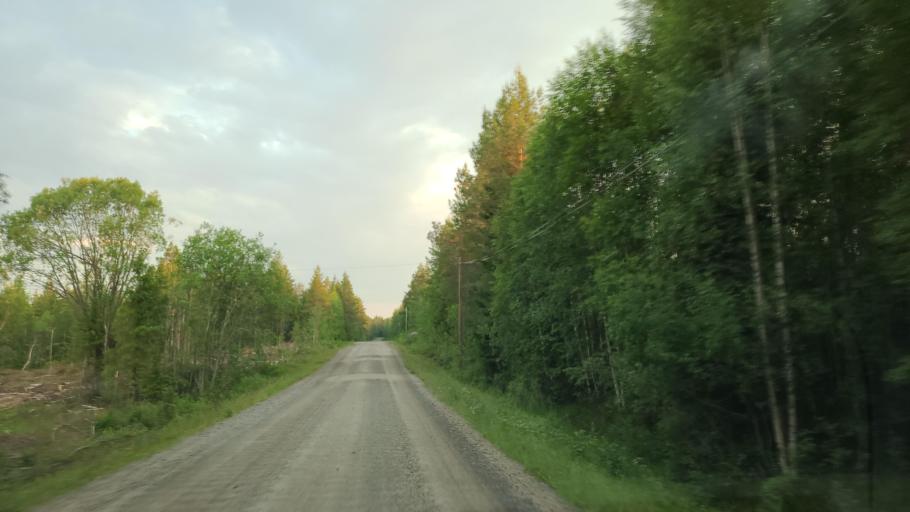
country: SE
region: Vaesterbotten
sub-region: Robertsfors Kommun
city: Robertsfors
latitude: 64.0759
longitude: 20.8857
